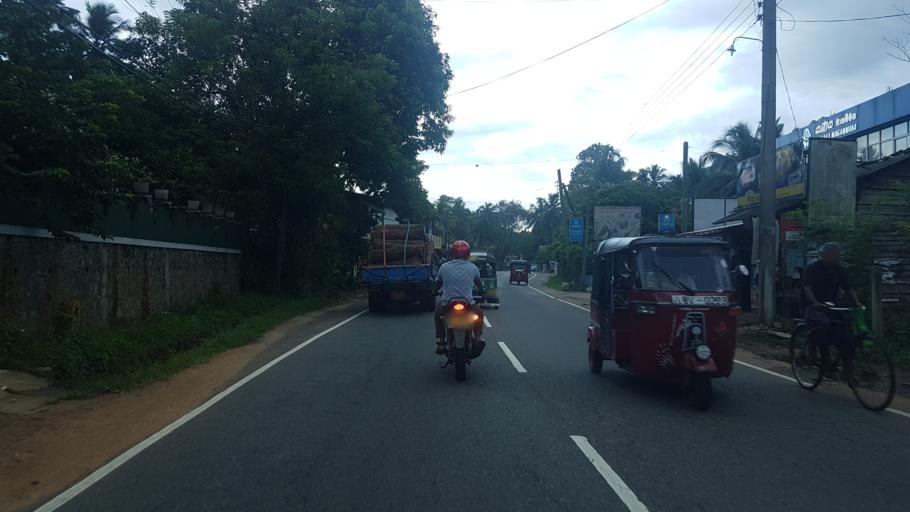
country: LK
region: Western
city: Hanwella Ihala
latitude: 7.0147
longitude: 80.2632
